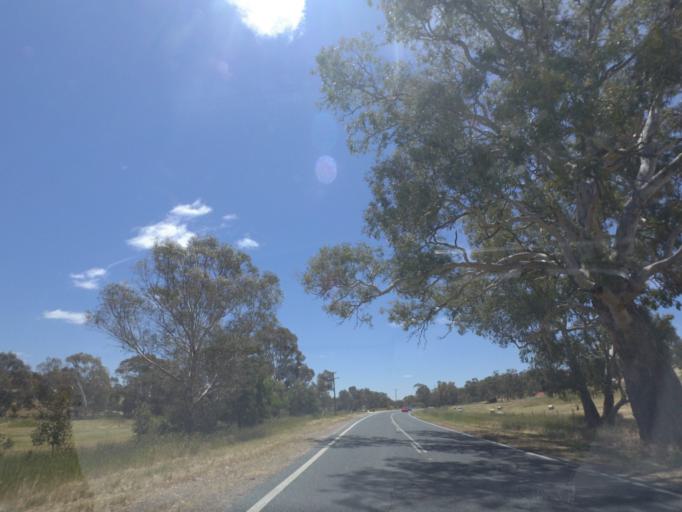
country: AU
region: Victoria
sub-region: Mount Alexander
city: Castlemaine
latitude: -37.1884
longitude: 144.1487
